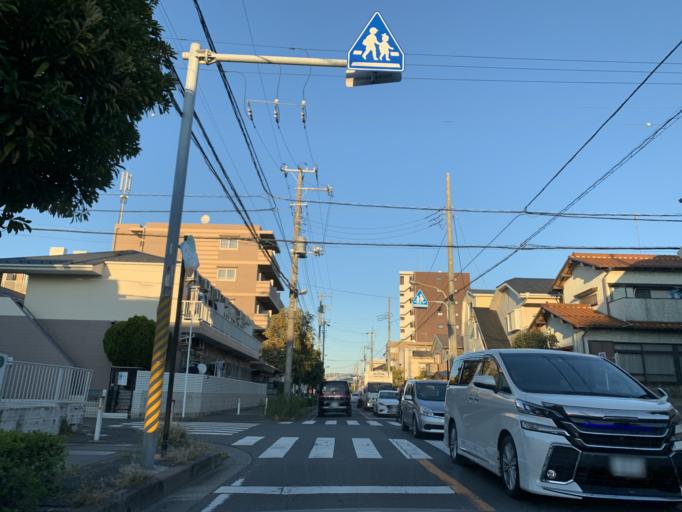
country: JP
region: Tokyo
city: Urayasu
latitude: 35.6879
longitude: 139.9308
